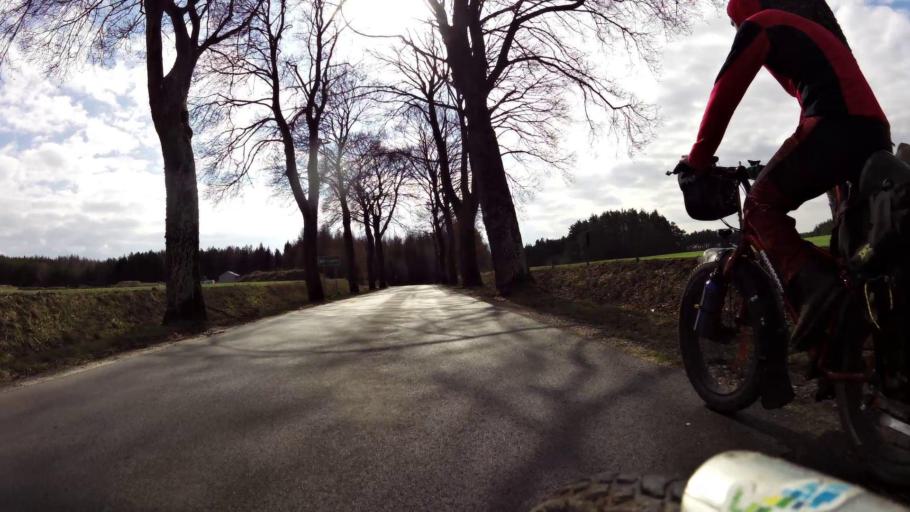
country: PL
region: Pomeranian Voivodeship
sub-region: Powiat bytowski
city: Kolczyglowy
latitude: 54.2086
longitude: 17.2354
